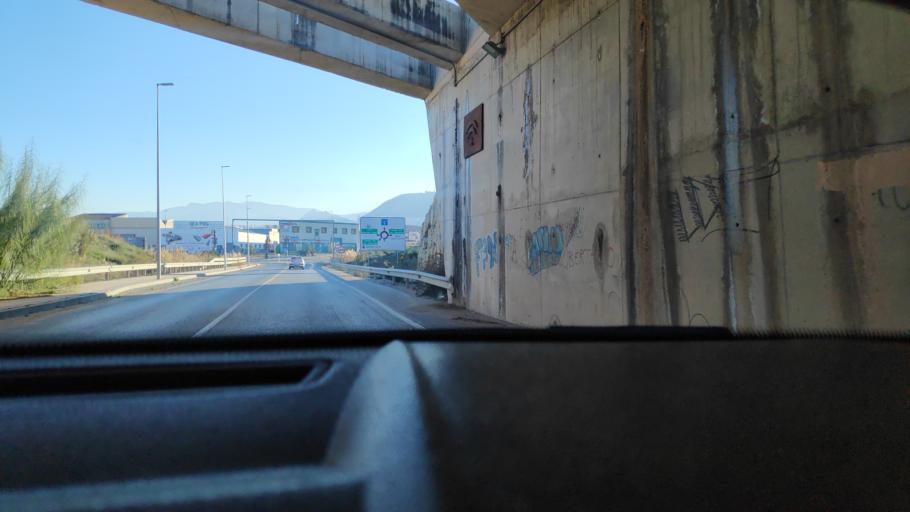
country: ES
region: Andalusia
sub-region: Provincia de Jaen
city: Jaen
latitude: 37.8038
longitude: -3.7881
